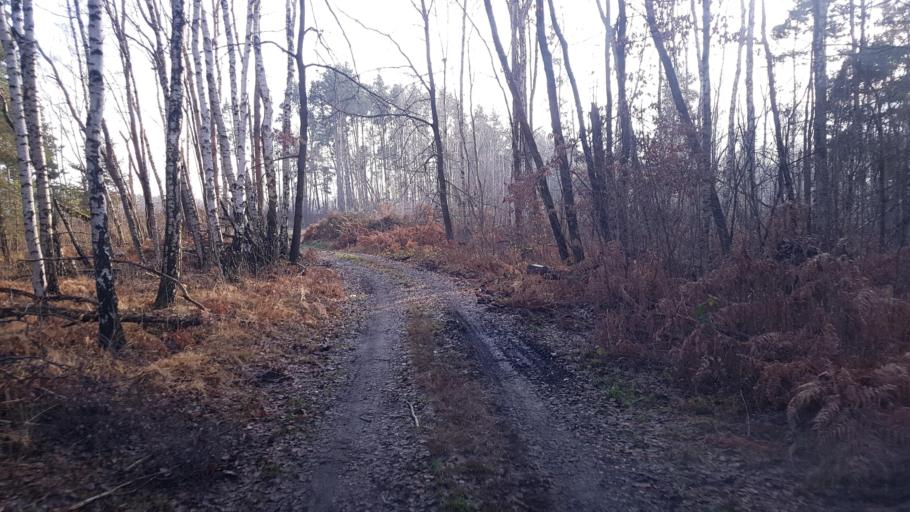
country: DE
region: Brandenburg
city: Plessa
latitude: 51.5228
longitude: 13.6828
